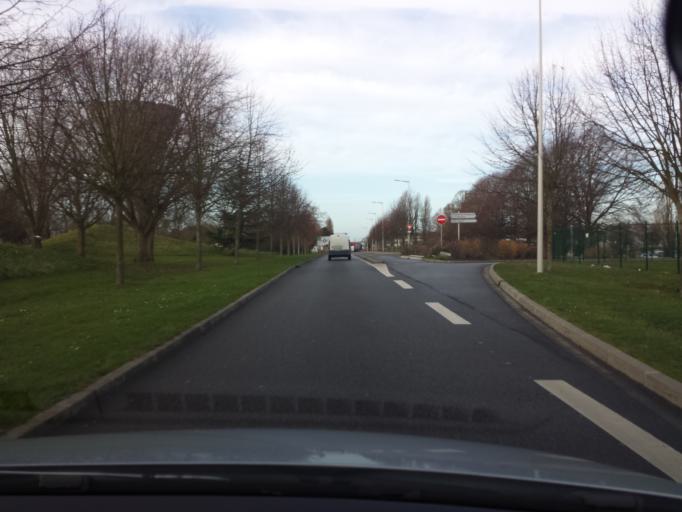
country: FR
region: Haute-Normandie
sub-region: Departement de l'Eure
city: Evreux
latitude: 49.0161
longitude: 1.1743
